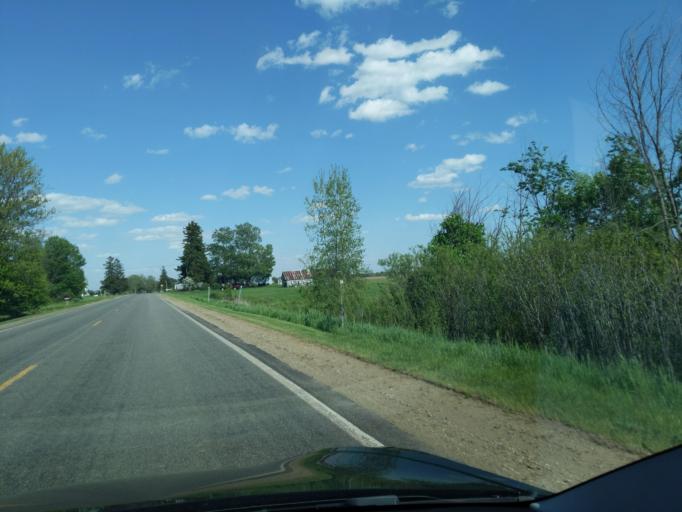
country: US
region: Michigan
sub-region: Ionia County
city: Lake Odessa
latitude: 42.7845
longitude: -85.1707
